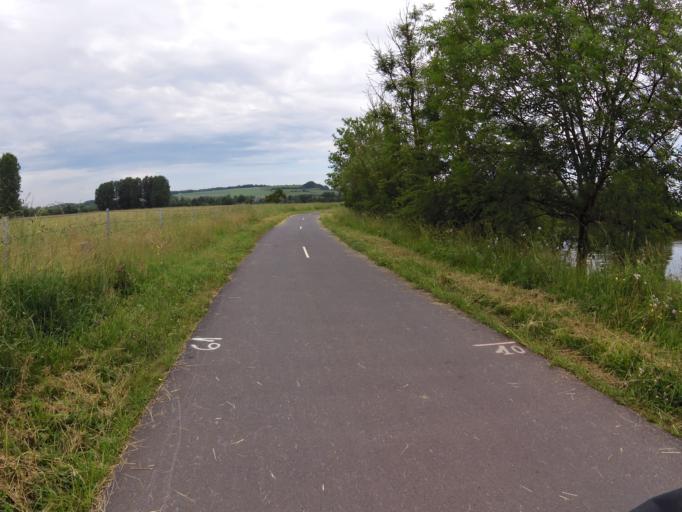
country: FR
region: Champagne-Ardenne
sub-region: Departement des Ardennes
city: Donchery
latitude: 49.6940
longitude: 4.8607
